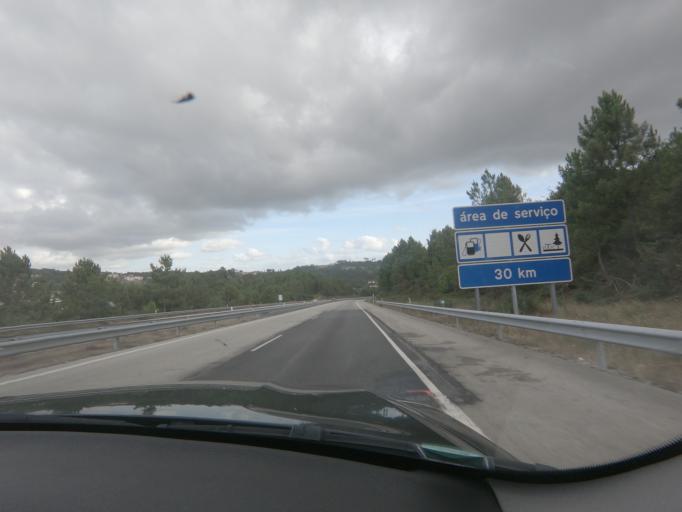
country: PT
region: Viseu
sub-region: Castro Daire
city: Castro Daire
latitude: 40.9131
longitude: -7.9092
